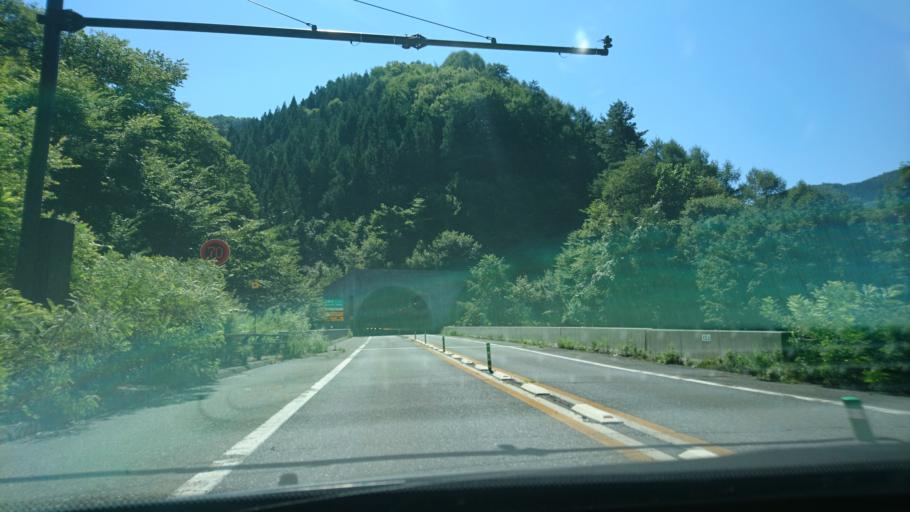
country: JP
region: Iwate
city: Tono
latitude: 39.2459
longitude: 141.6361
